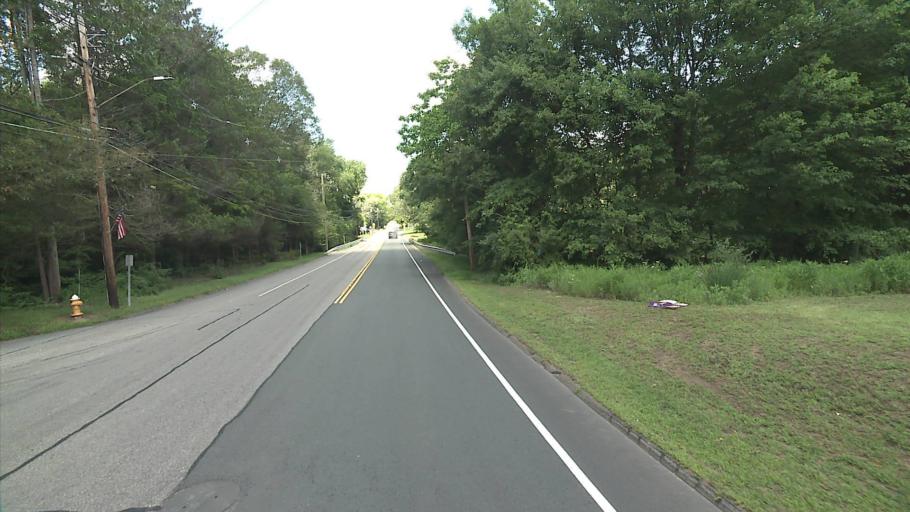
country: US
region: Connecticut
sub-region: Middlesex County
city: Deep River Center
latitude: 41.3699
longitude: -72.4280
